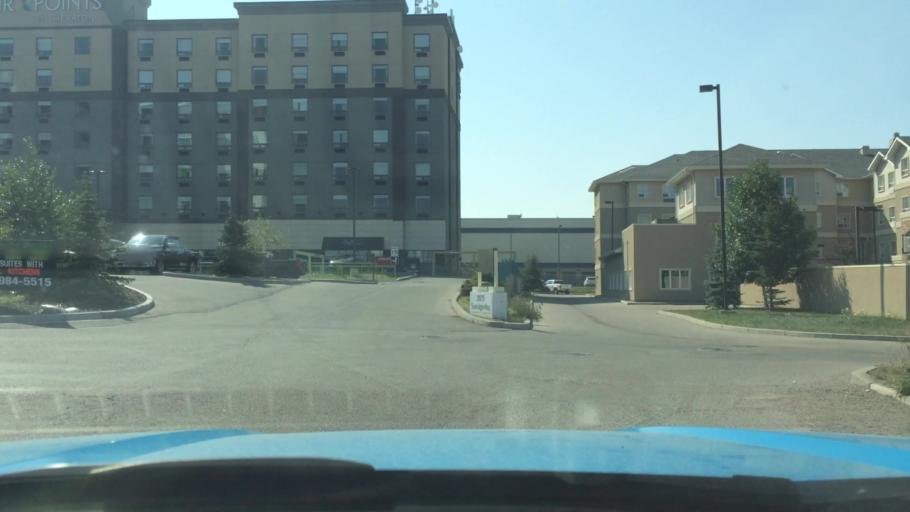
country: CA
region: Alberta
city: Calgary
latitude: 51.0719
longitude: -114.0001
